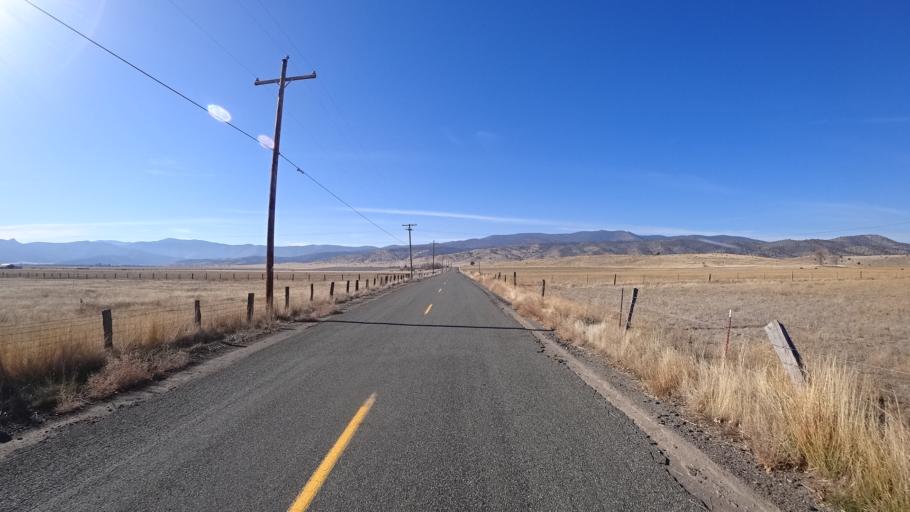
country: US
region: California
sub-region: Siskiyou County
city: Montague
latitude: 41.5745
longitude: -122.5274
